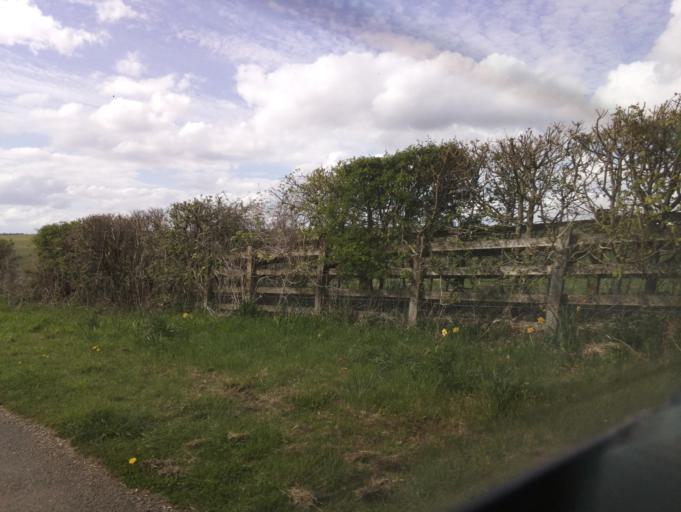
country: GB
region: England
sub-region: Hampshire
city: Romsey
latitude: 51.0381
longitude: -1.5148
